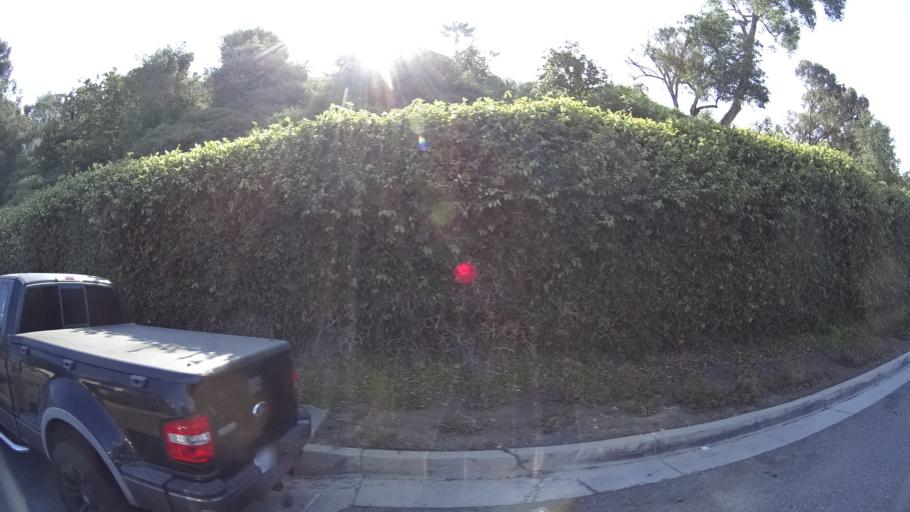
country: US
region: California
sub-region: Orange County
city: San Juan Capistrano
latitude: 33.4612
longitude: -117.6507
